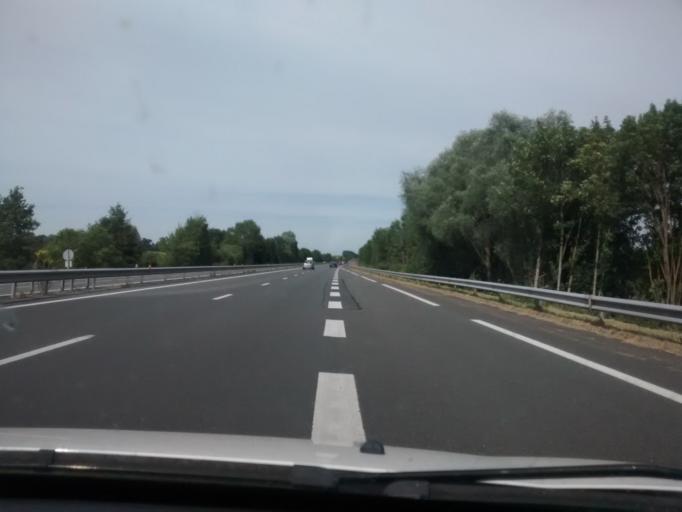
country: FR
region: Pays de la Loire
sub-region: Departement de la Sarthe
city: Etival-les-le-Mans
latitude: 47.9827
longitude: 0.0557
